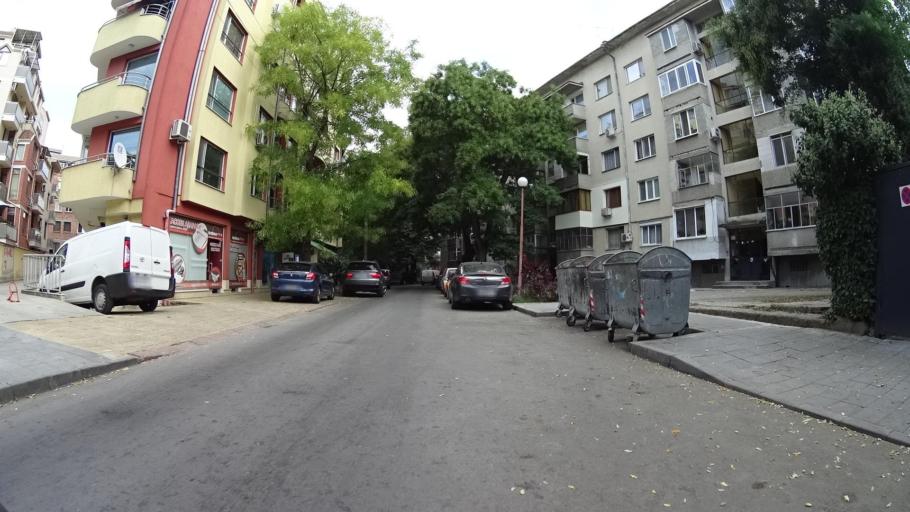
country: BG
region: Plovdiv
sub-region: Obshtina Plovdiv
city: Plovdiv
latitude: 42.1555
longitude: 24.7399
